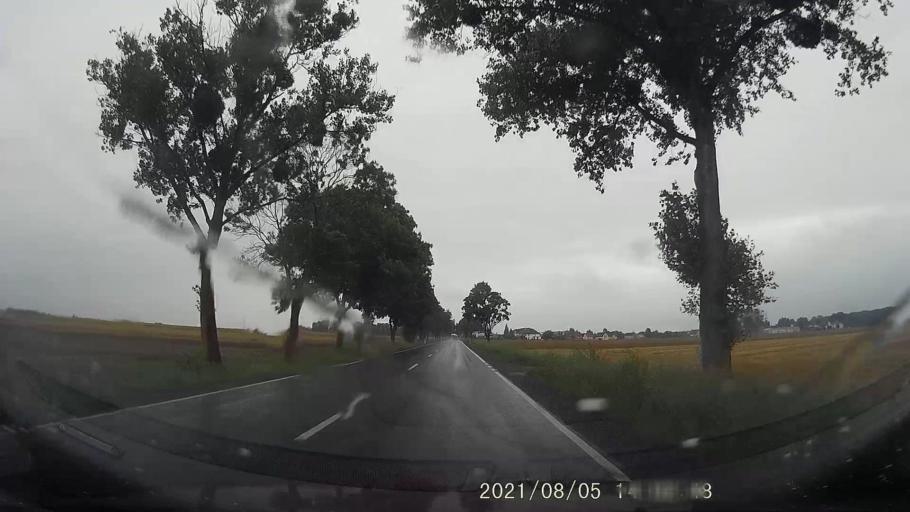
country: PL
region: Opole Voivodeship
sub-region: Powiat krapkowicki
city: Strzeleczki
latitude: 50.4567
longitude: 17.8675
